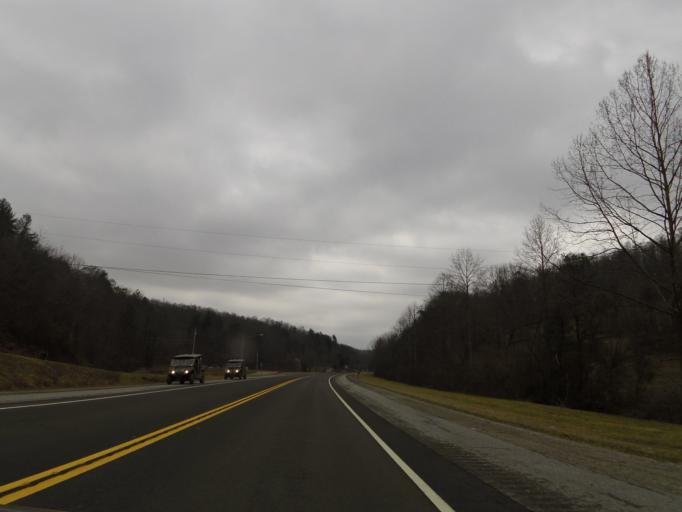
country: US
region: Tennessee
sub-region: Scott County
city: Huntsville
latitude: 36.4141
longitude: -84.4671
